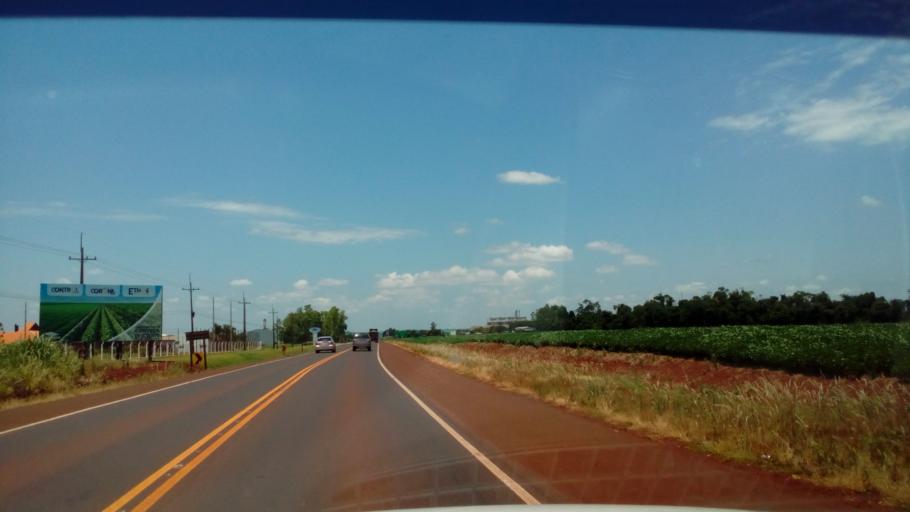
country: PY
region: Alto Parana
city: Santa Rita
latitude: -25.8722
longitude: -55.1179
